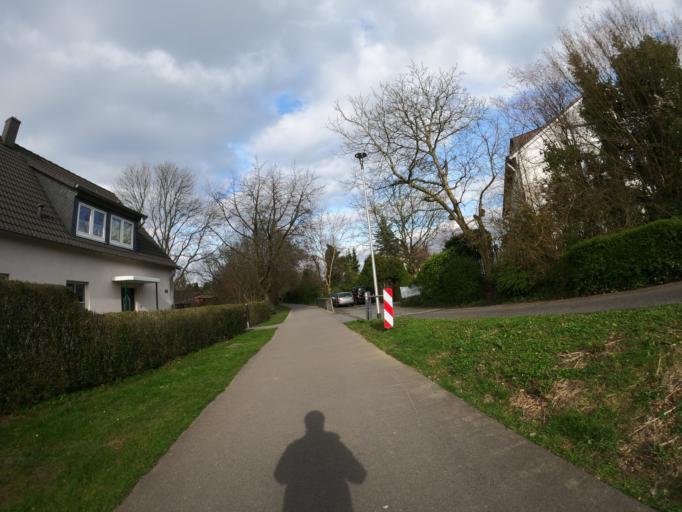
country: DE
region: North Rhine-Westphalia
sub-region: Regierungsbezirk Dusseldorf
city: Solingen
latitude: 51.1973
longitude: 7.0721
